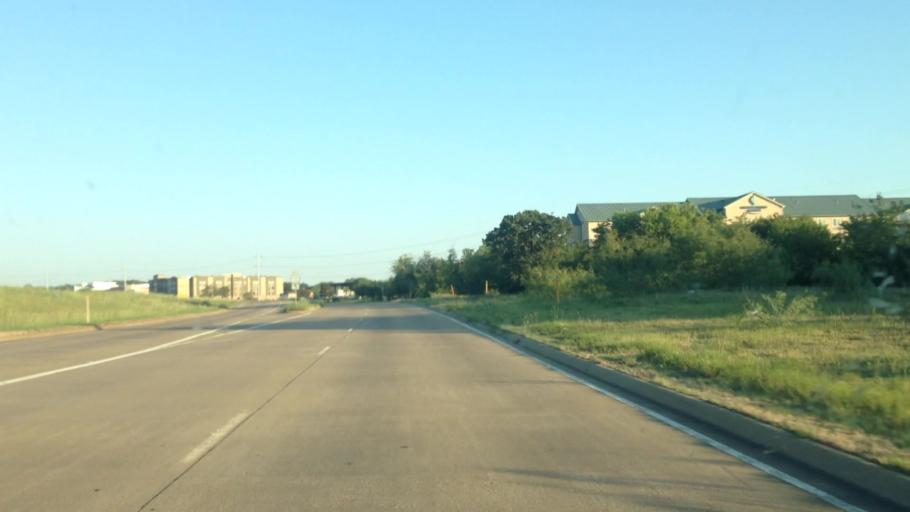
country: US
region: Texas
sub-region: Denton County
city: Trophy Club
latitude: 32.9841
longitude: -97.1684
